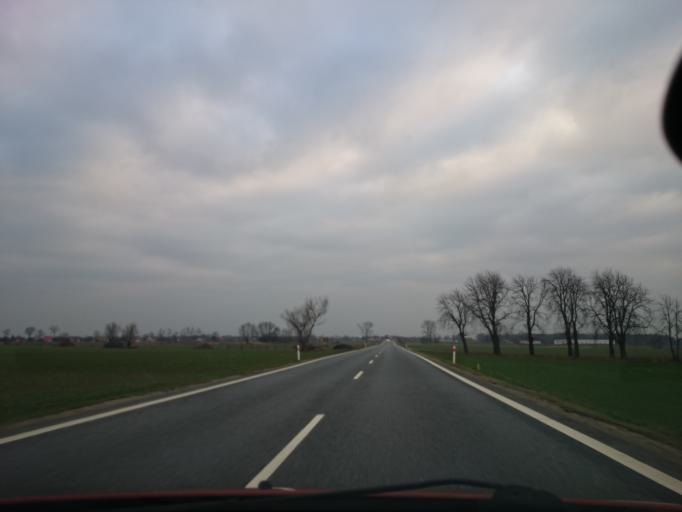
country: PL
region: Opole Voivodeship
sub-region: Powiat nyski
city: Sidzina
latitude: 50.5822
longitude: 17.4645
